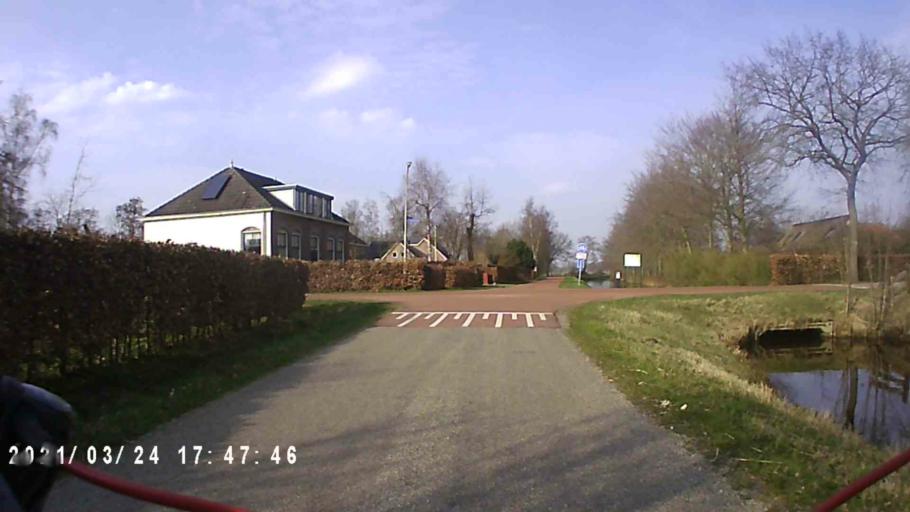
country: NL
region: Groningen
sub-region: Gemeente Leek
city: Leek
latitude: 53.1162
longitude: 6.3353
